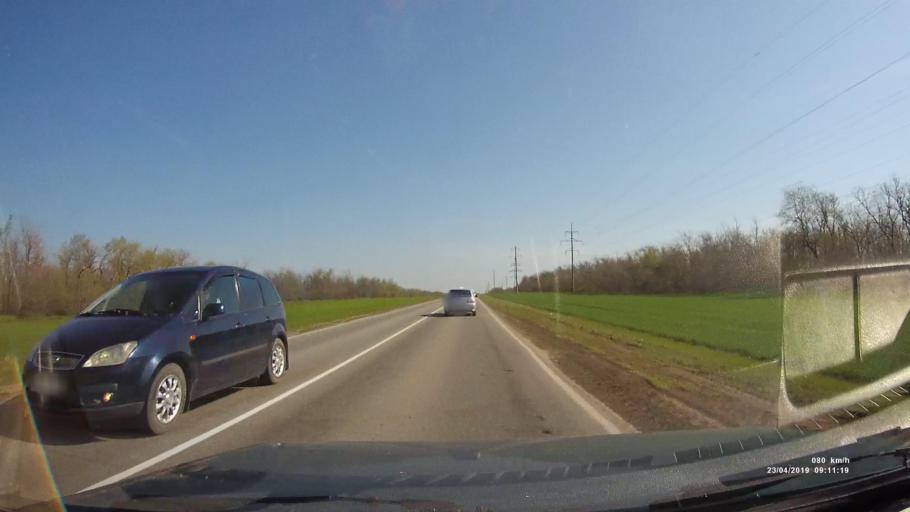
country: RU
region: Rostov
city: Proletarsk
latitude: 46.5955
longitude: 41.6272
